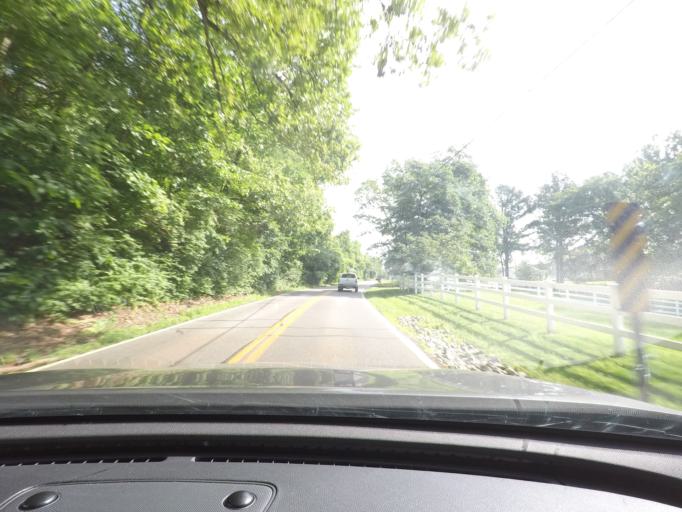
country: US
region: Missouri
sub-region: Saint Louis County
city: Town and Country
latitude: 38.6179
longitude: -90.4860
